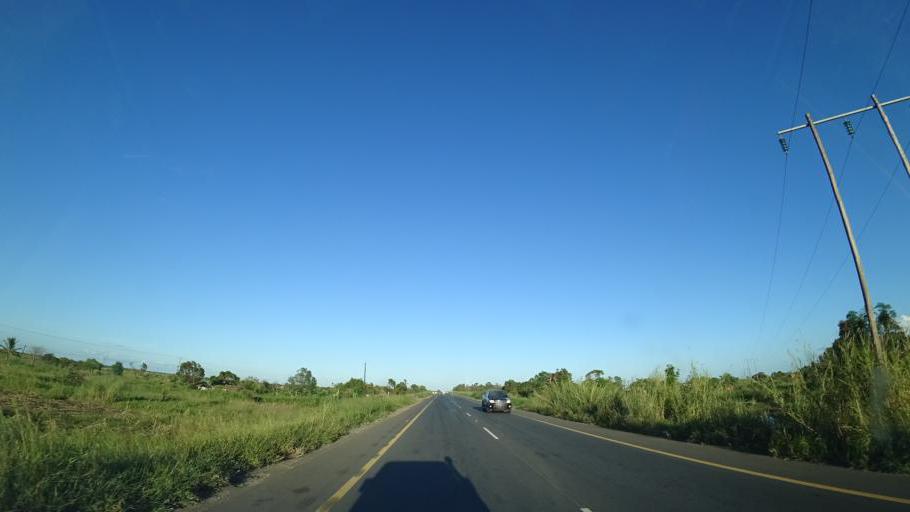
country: MZ
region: Sofala
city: Dondo
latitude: -19.3342
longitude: 34.3232
